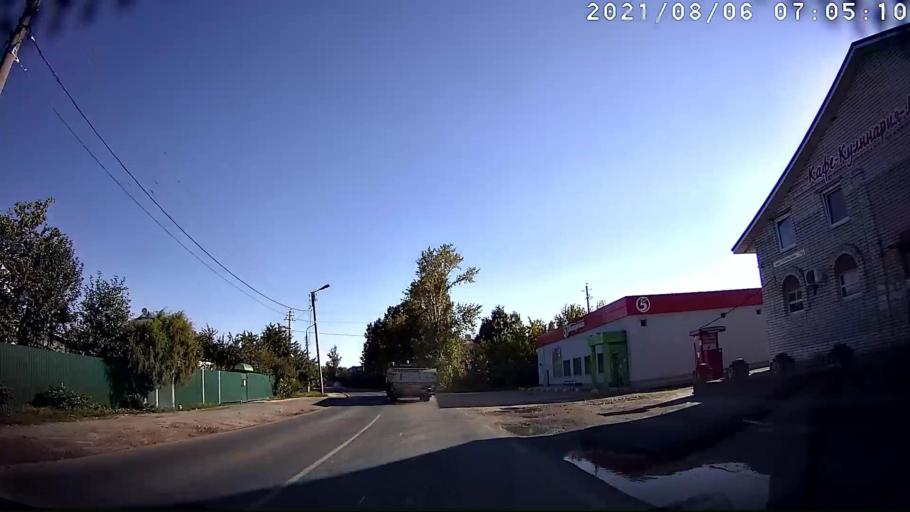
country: RU
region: Mariy-El
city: Yoshkar-Ola
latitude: 56.5518
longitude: 47.9859
